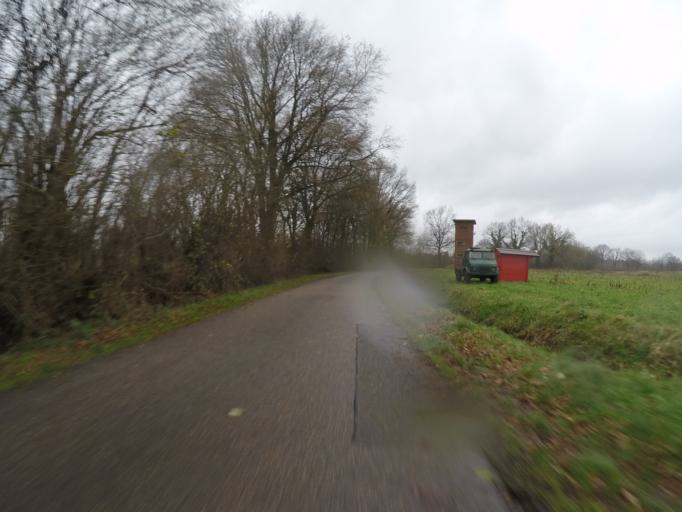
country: DE
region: Schleswig-Holstein
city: Bilsen
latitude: 53.7241
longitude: 9.8612
